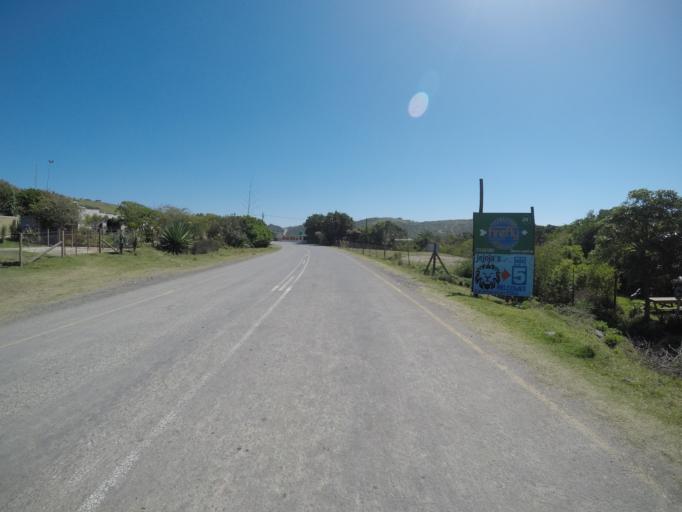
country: ZA
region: Eastern Cape
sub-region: OR Tambo District Municipality
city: Libode
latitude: -31.9852
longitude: 29.1486
